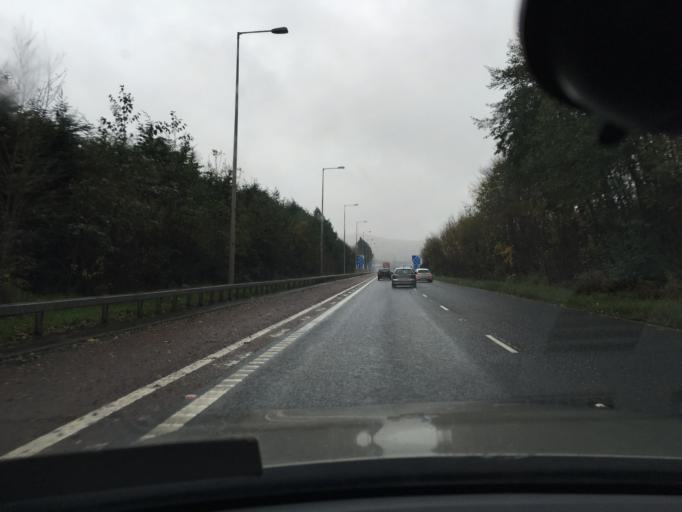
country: GB
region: Northern Ireland
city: Carnmoney
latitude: 54.6775
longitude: -5.9776
